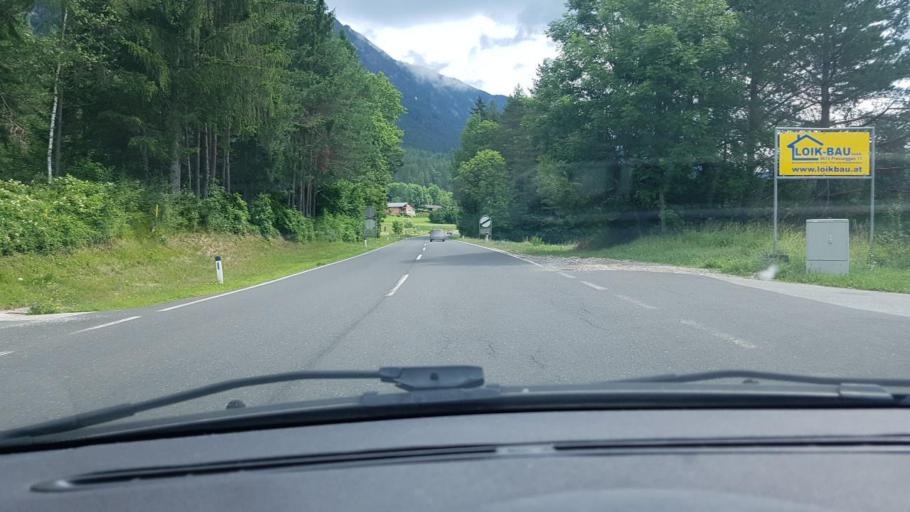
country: AT
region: Carinthia
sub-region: Politischer Bezirk Hermagor
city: Hermagor
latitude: 46.6307
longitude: 13.4576
